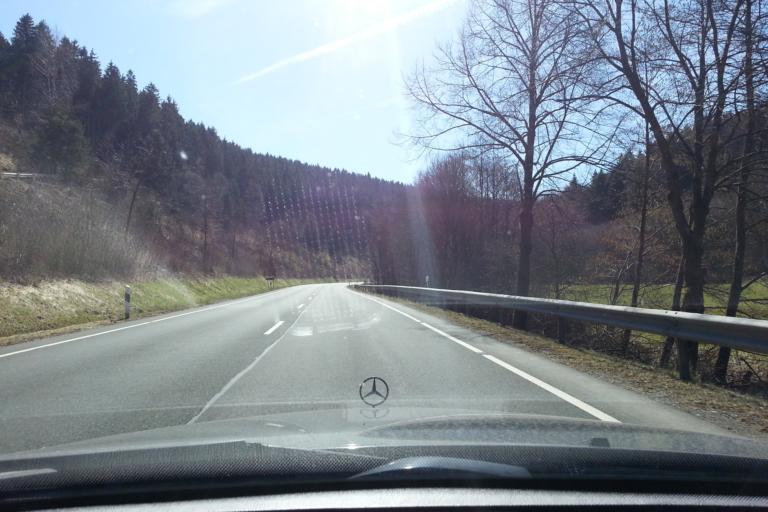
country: DE
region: North Rhine-Westphalia
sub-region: Regierungsbezirk Arnsberg
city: Bad Fredeburg
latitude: 51.2424
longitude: 8.3588
